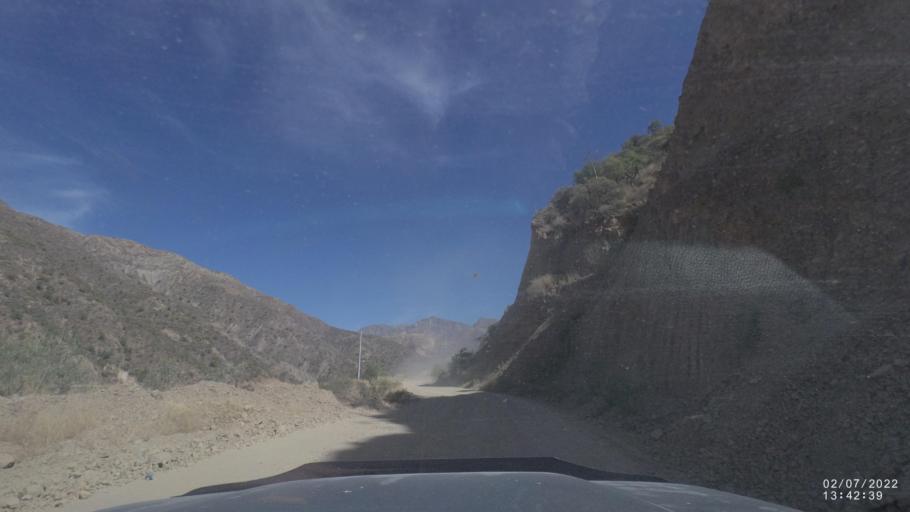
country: BO
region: Cochabamba
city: Irpa Irpa
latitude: -17.8011
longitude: -66.3561
